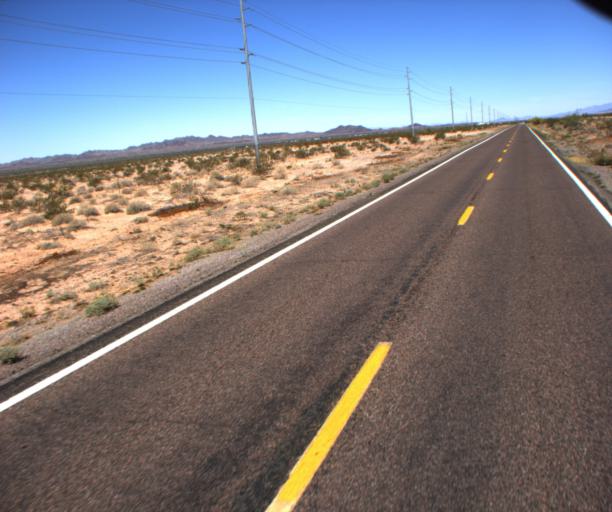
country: US
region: Arizona
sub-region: La Paz County
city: Quartzsite
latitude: 33.8930
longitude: -113.9627
